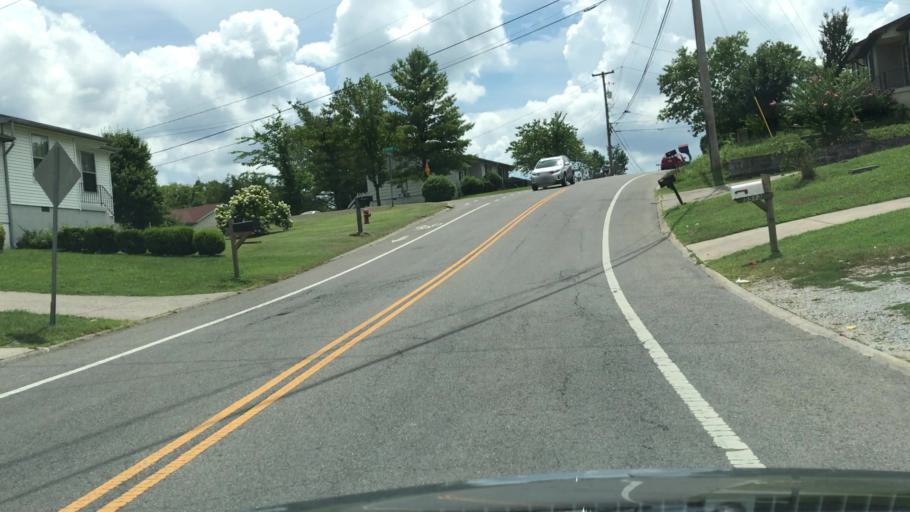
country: US
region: Tennessee
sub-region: Williamson County
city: Brentwood Estates
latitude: 36.0475
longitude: -86.7029
